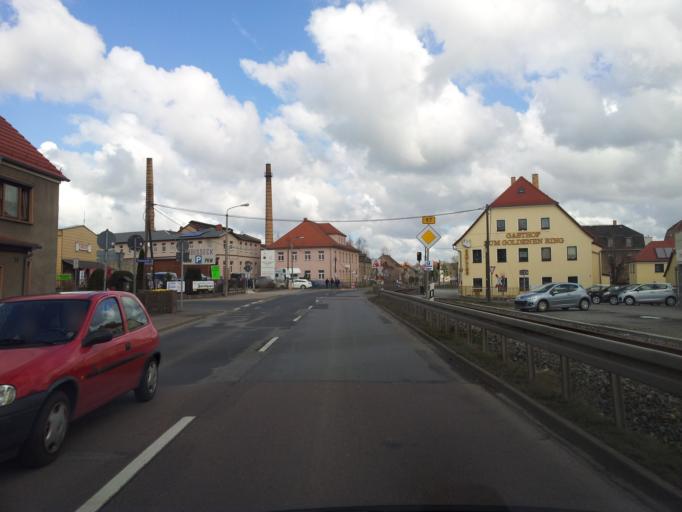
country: DE
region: Saxony
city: Ottendorf-Okrilla
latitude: 51.1928
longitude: 13.8344
